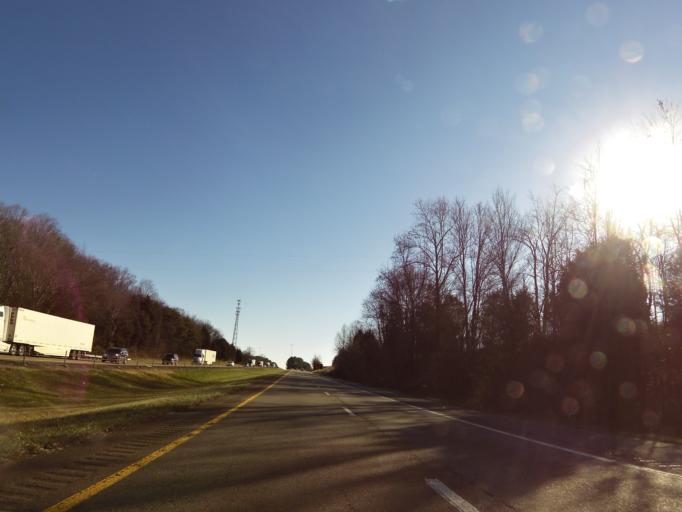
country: US
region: Tennessee
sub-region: Cocke County
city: Newport
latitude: 35.9728
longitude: -83.2681
